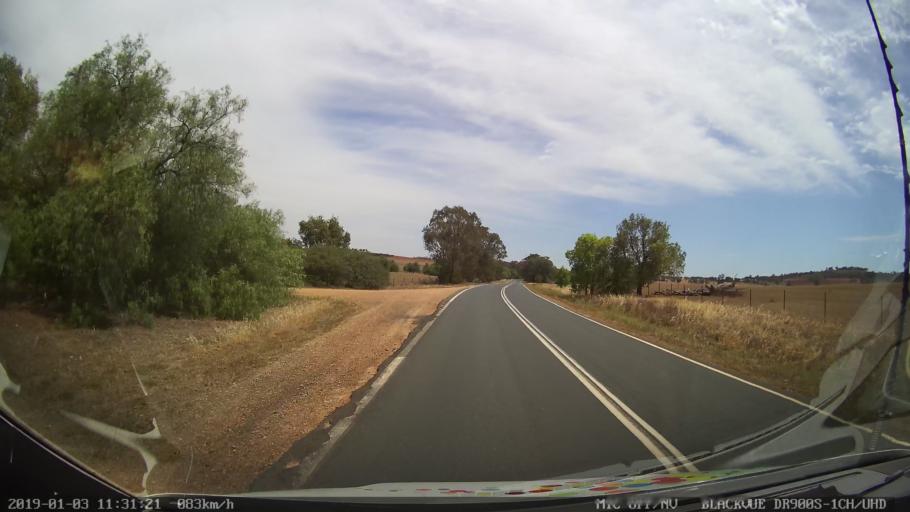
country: AU
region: New South Wales
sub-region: Weddin
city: Grenfell
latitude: -33.9715
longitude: 148.1842
